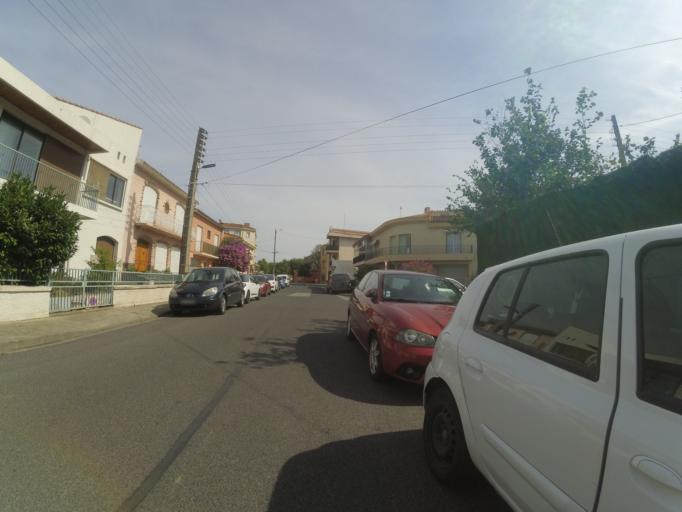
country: FR
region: Languedoc-Roussillon
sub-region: Departement des Pyrenees-Orientales
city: Ille-sur-Tet
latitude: 42.6694
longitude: 2.6220
